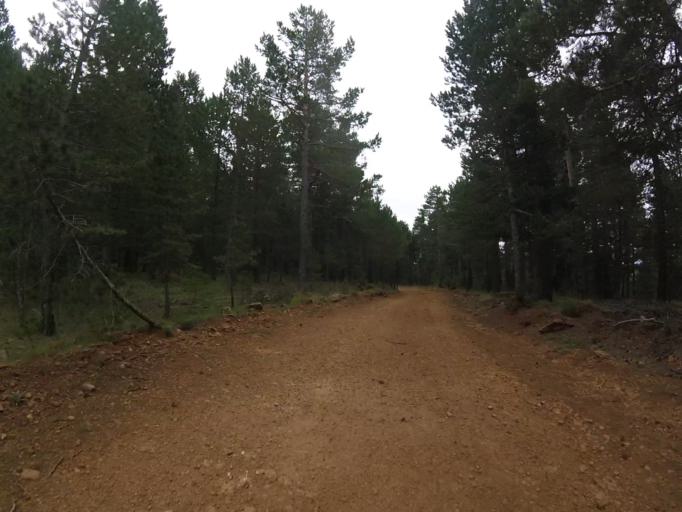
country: ES
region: Aragon
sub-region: Provincia de Teruel
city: Valdelinares
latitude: 40.3700
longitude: -0.6202
